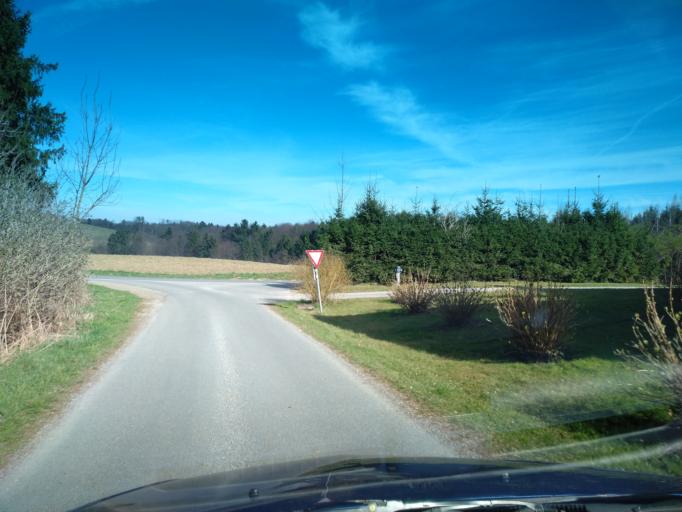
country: AT
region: Styria
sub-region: Politischer Bezirk Deutschlandsberg
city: Unterbergla
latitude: 46.7949
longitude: 15.3125
